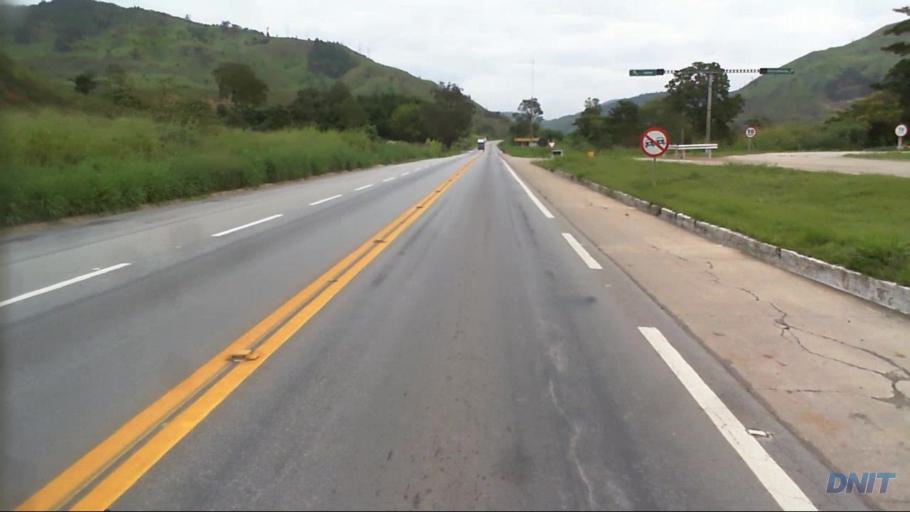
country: BR
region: Minas Gerais
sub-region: Timoteo
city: Timoteo
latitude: -19.5955
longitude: -42.7435
